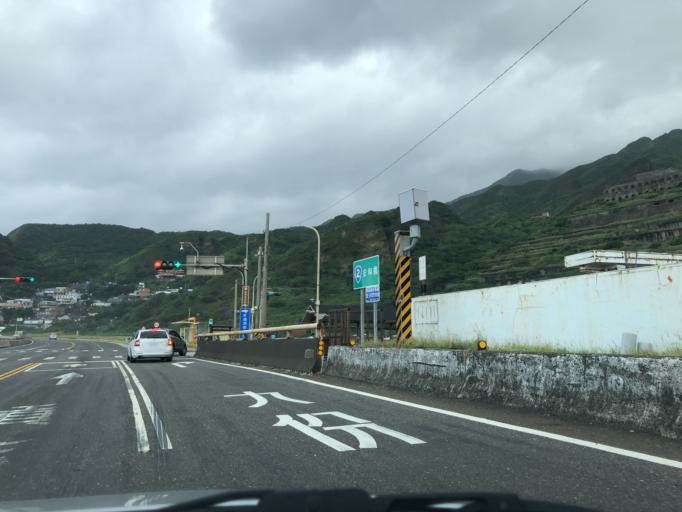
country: TW
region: Taiwan
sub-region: Keelung
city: Keelung
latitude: 25.1227
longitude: 121.8633
